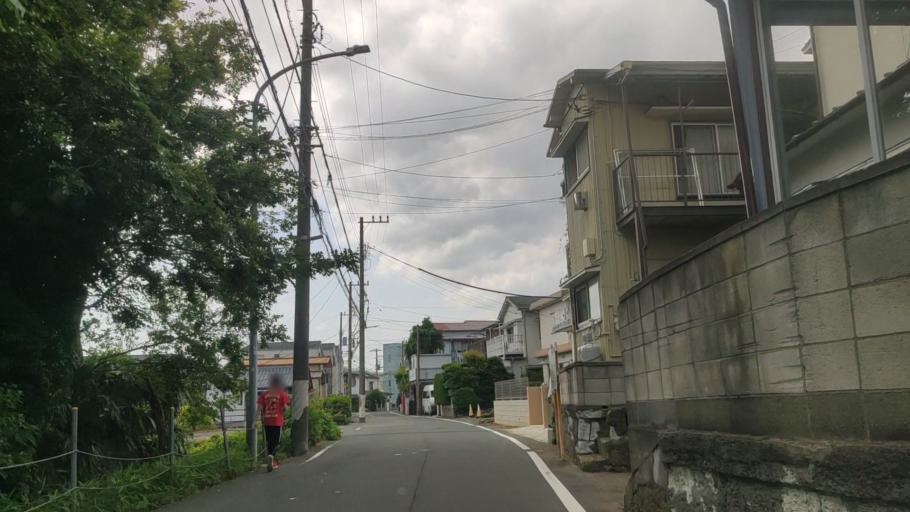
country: JP
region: Kanagawa
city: Yokohama
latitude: 35.4291
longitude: 139.6271
